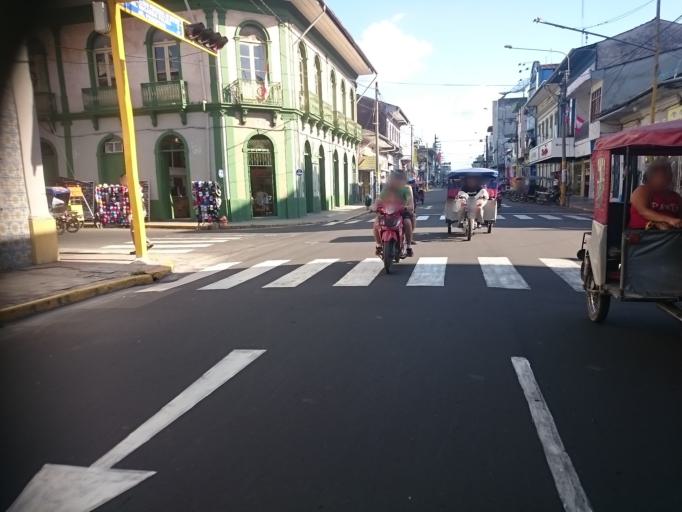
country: PE
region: Loreto
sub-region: Provincia de Maynas
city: Iquitos
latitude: -3.7548
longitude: -73.2470
